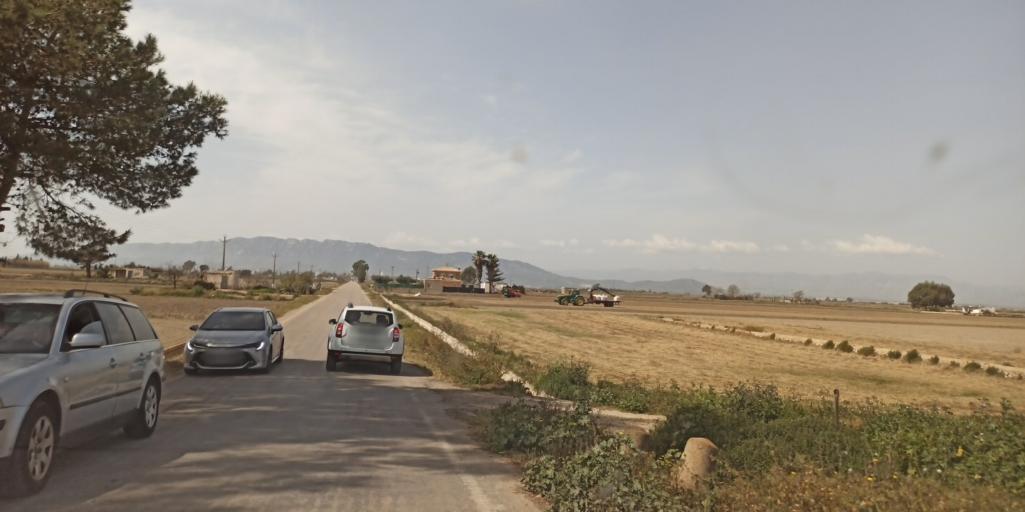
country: ES
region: Catalonia
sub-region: Provincia de Tarragona
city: Deltebre
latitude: 40.6471
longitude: 0.7073
